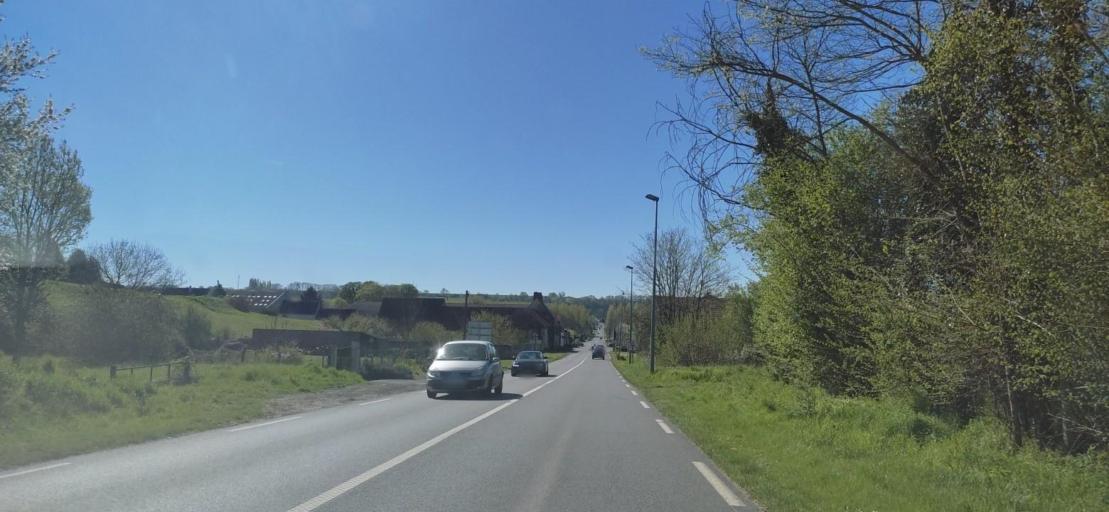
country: FR
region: Picardie
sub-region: Departement de l'Oise
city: Villers-sur-Coudun
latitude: 49.4723
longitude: 2.7552
